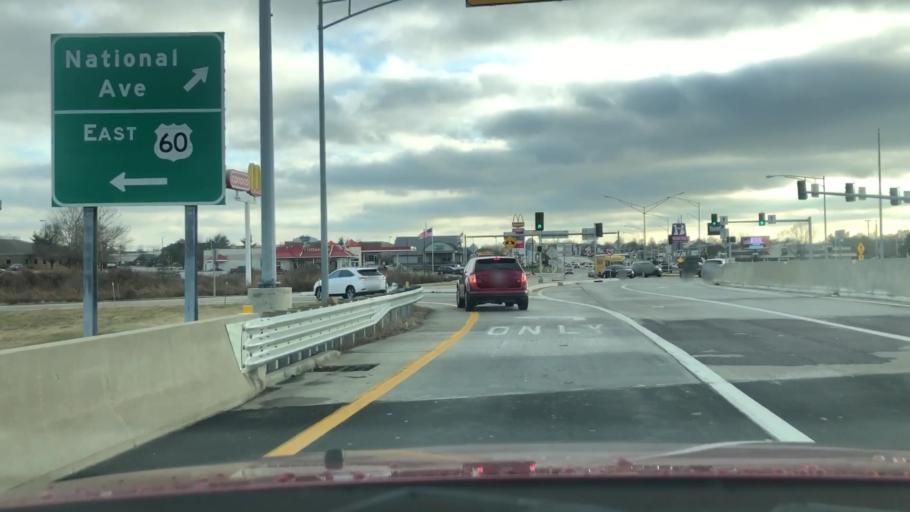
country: US
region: Missouri
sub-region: Greene County
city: Springfield
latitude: 37.1416
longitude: -93.2780
